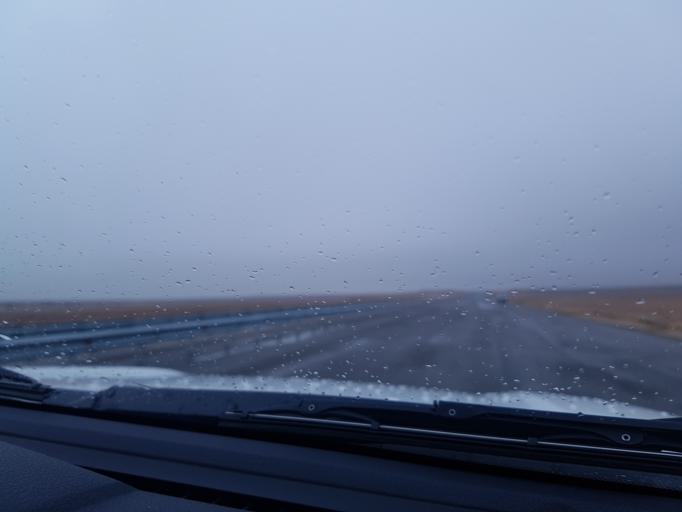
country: TM
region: Balkan
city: Balkanabat
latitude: 39.9644
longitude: 53.8139
